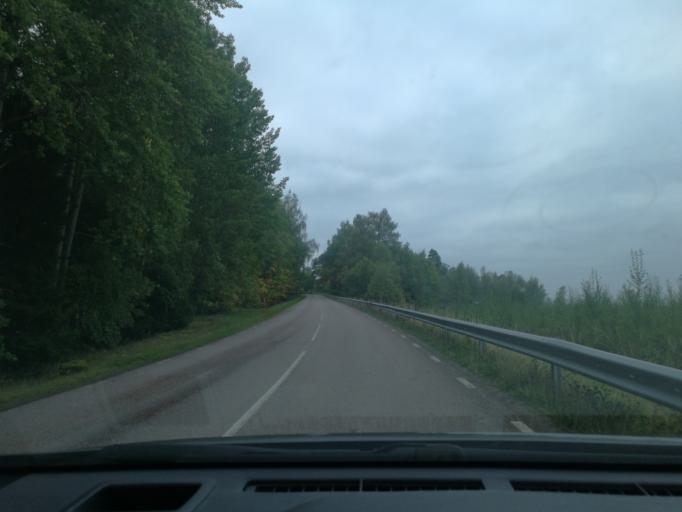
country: SE
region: Vaestmanland
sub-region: Vasteras
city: Tillberga
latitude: 59.6996
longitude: 16.6432
